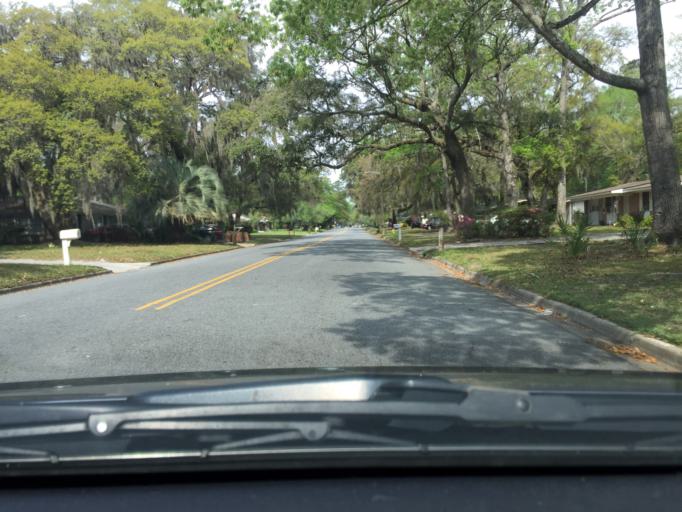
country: US
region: Georgia
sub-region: Chatham County
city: Montgomery
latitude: 31.9850
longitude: -81.1386
